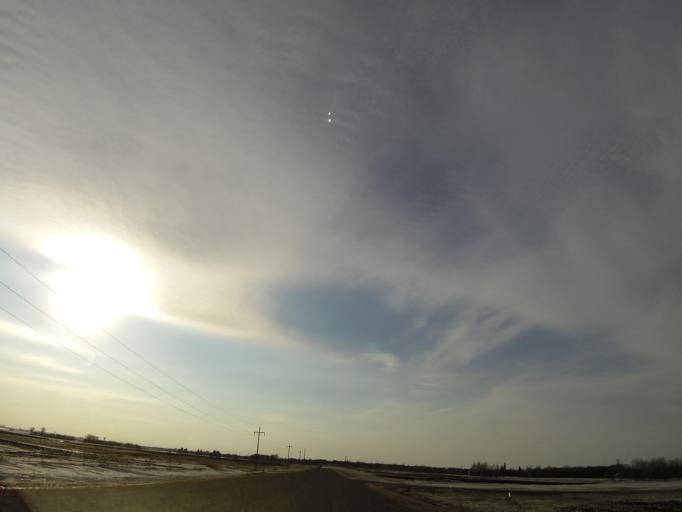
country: US
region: North Dakota
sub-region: Walsh County
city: Grafton
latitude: 48.4198
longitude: -97.3678
